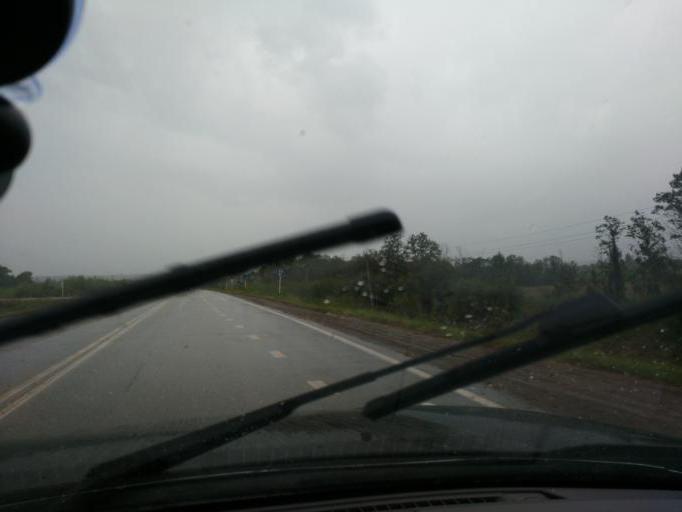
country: RU
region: Perm
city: Barda
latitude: 56.9440
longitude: 55.6171
